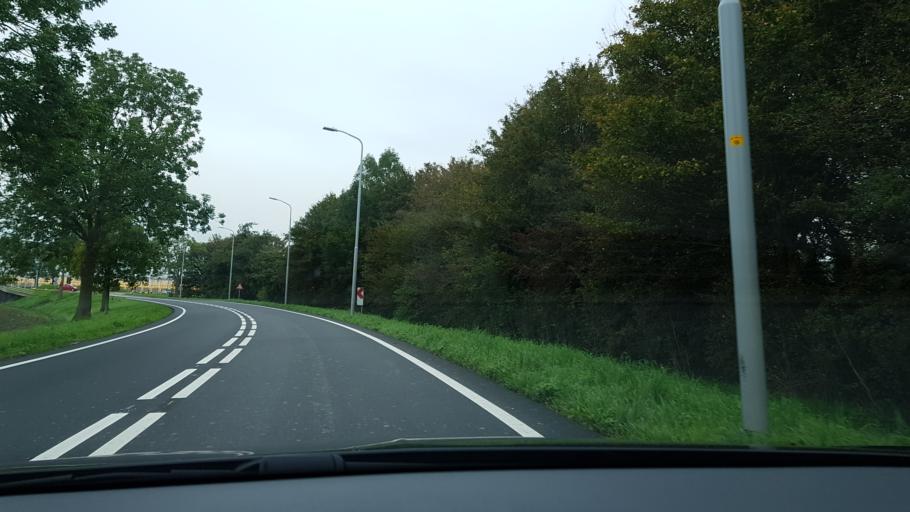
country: NL
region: South Holland
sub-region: Gemeente Kaag en Braassem
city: Leimuiden
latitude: 52.2392
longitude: 4.6790
